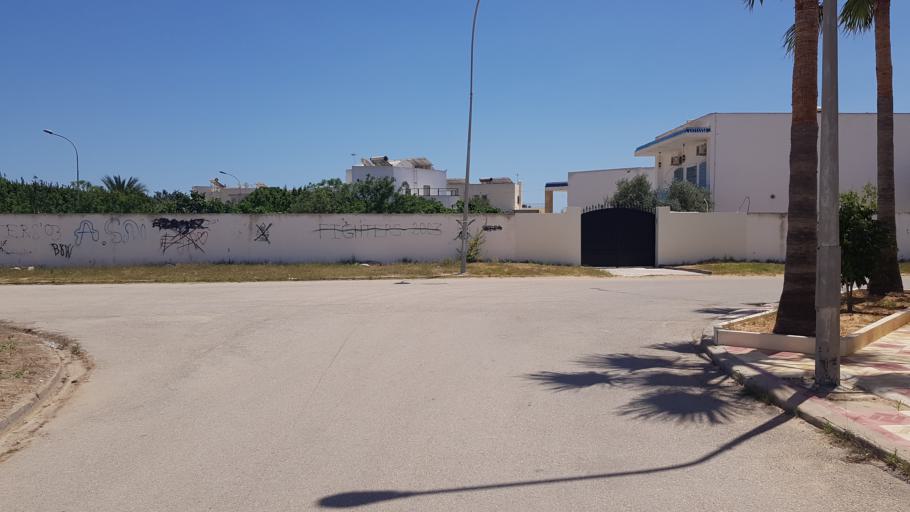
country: TN
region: Safaqis
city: Al Qarmadah
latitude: 34.8269
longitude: 10.7606
